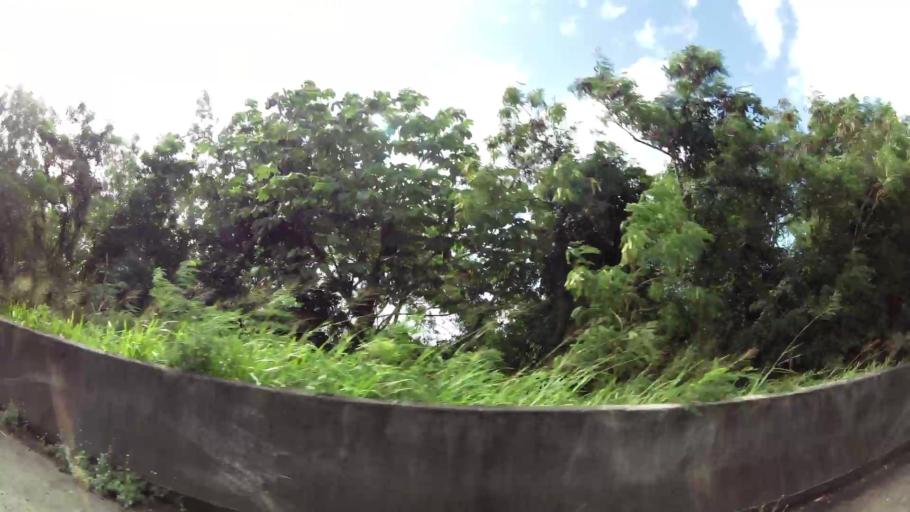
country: MQ
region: Martinique
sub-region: Martinique
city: Les Trois-Ilets
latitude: 14.4819
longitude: -61.0049
